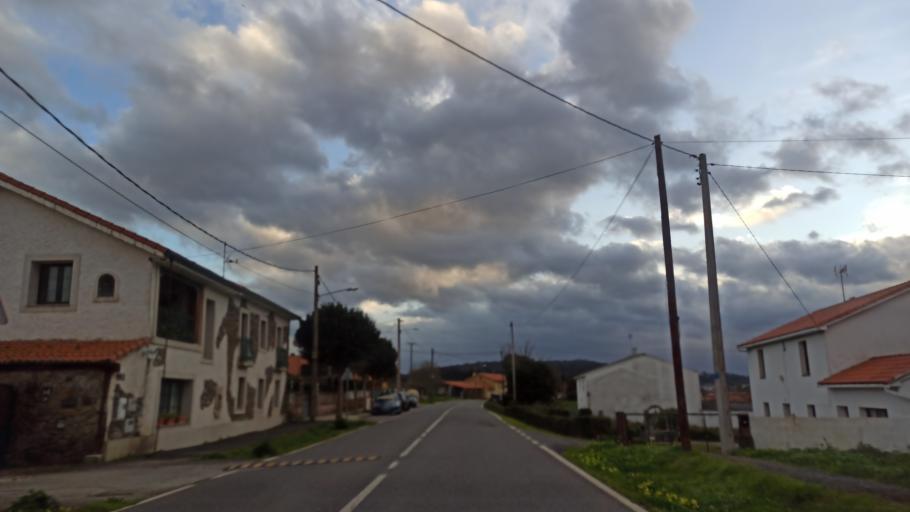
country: ES
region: Galicia
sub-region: Provincia da Coruna
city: Oleiros
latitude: 43.3857
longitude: -8.3216
